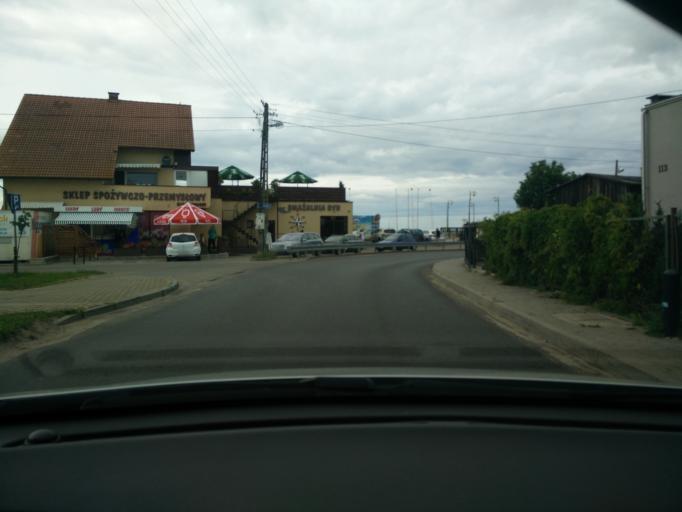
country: PL
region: Pomeranian Voivodeship
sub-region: Powiat pucki
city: Mosty
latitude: 54.6313
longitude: 18.4969
